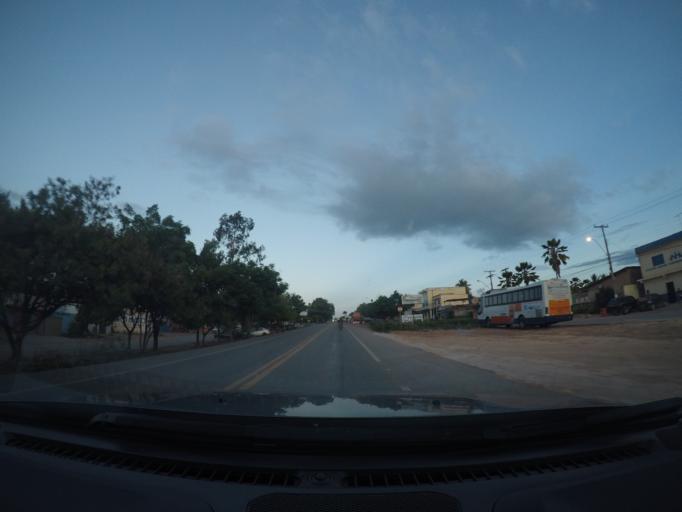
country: BR
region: Bahia
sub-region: Seabra
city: Seabra
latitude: -12.4279
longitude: -41.7738
